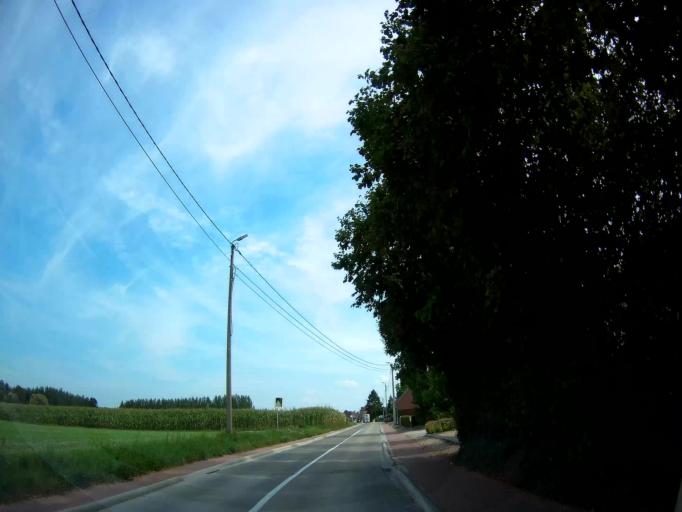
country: BE
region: Flanders
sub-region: Provincie Vlaams-Brabant
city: Zoutleeuw
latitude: 50.8265
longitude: 5.1272
